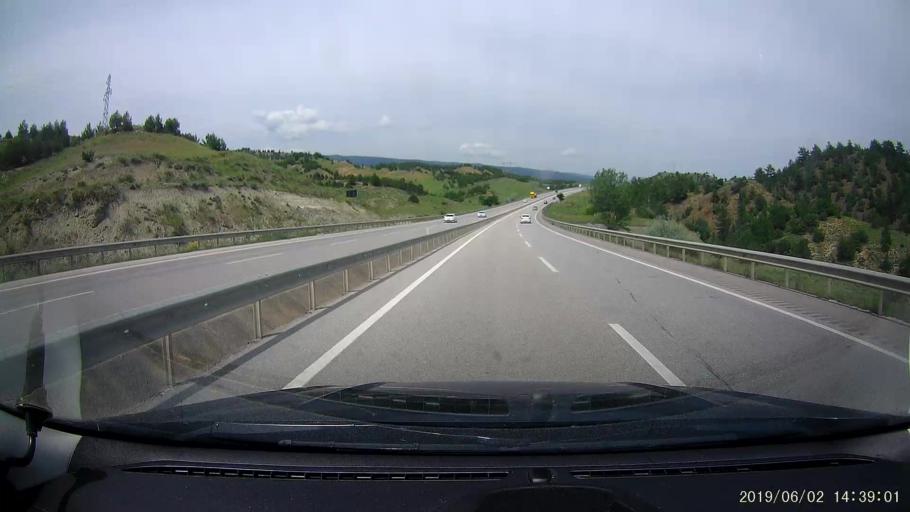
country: TR
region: Corum
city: Hacihamza
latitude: 41.0643
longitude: 34.2912
